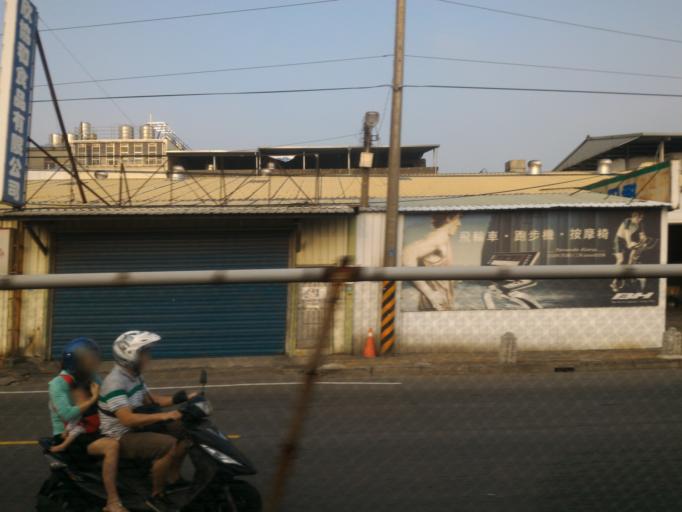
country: TW
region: Taiwan
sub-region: Taoyuan
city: Taoyuan
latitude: 24.9772
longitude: 121.3320
